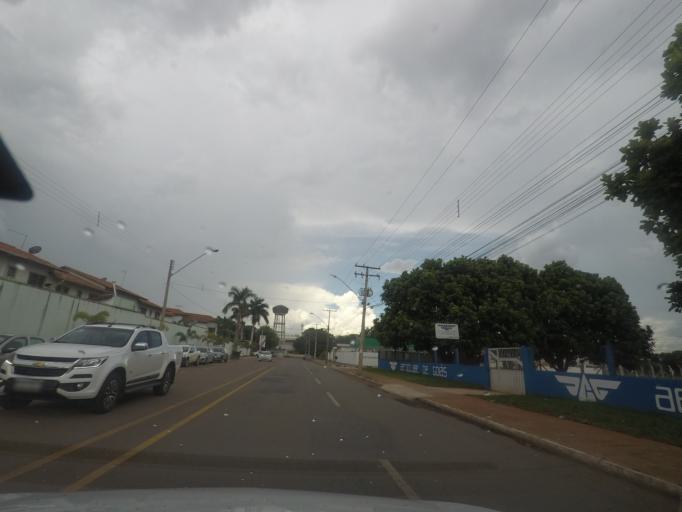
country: BR
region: Goias
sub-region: Goiania
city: Goiania
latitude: -16.6356
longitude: -49.2265
